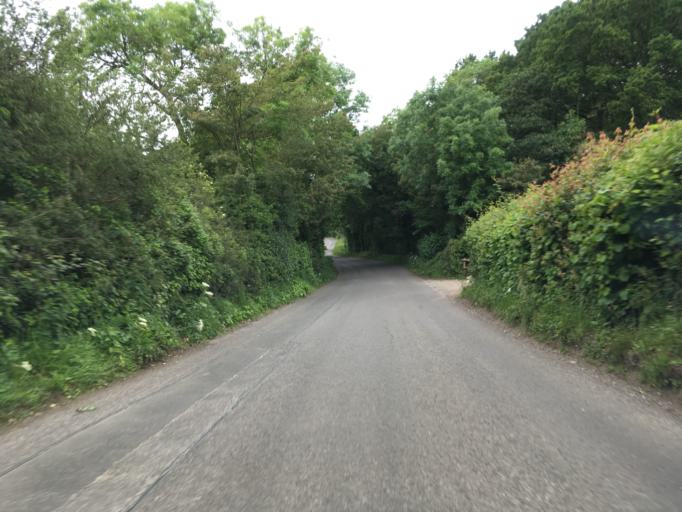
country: GB
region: England
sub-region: Wiltshire
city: Malmesbury
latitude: 51.5204
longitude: -2.0991
